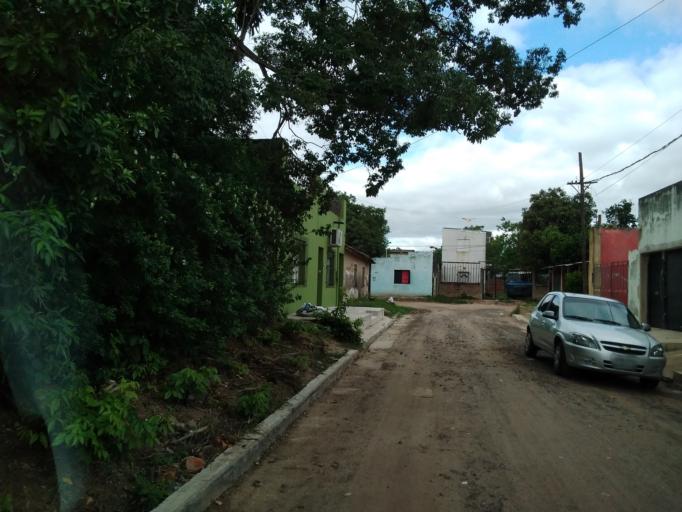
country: AR
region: Corrientes
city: Corrientes
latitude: -27.4739
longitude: -58.8079
